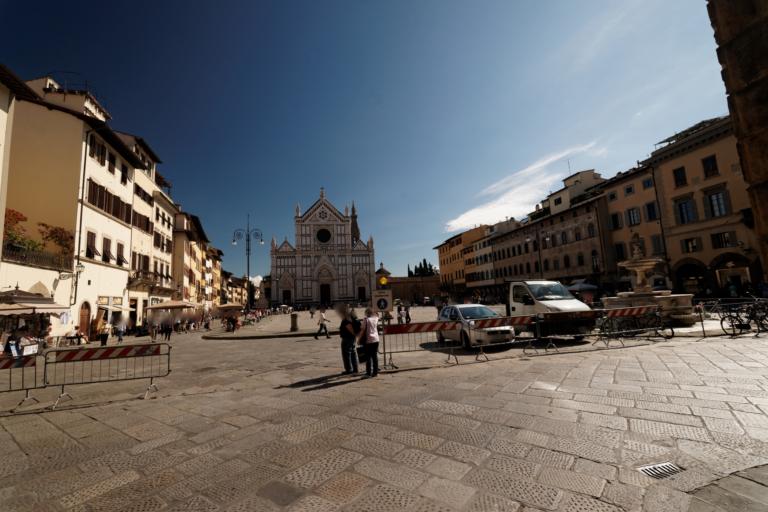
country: IT
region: Tuscany
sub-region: Province of Florence
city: Florence
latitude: 43.7692
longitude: 11.2607
